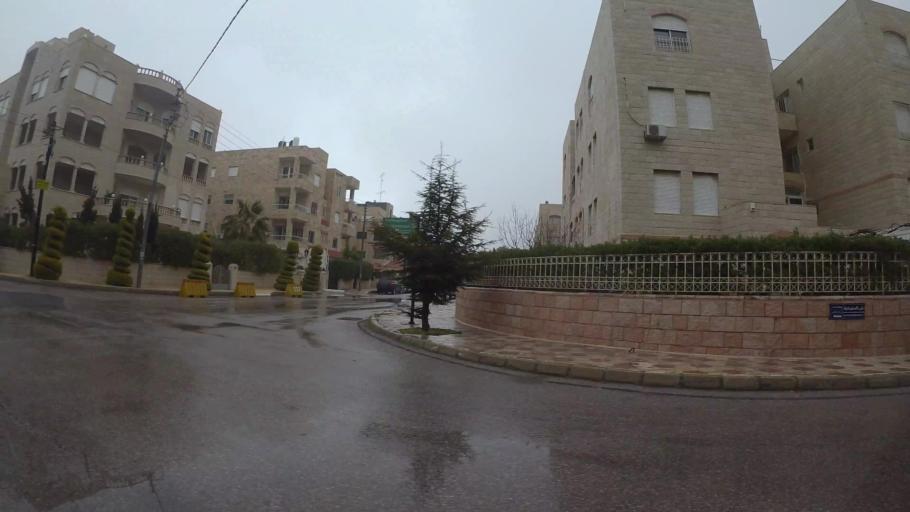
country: JO
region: Amman
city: Wadi as Sir
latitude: 31.9639
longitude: 35.8726
